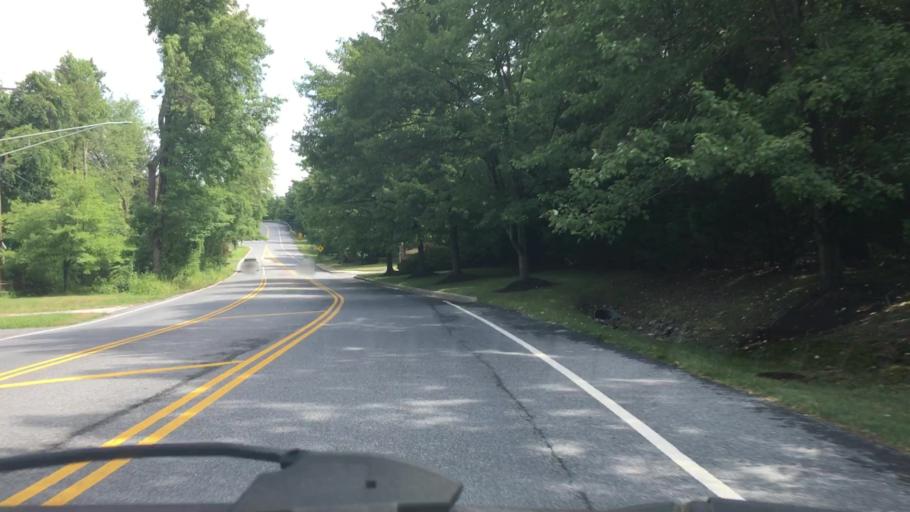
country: US
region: Maryland
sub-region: Anne Arundel County
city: Pasadena
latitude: 39.0969
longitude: -76.5779
